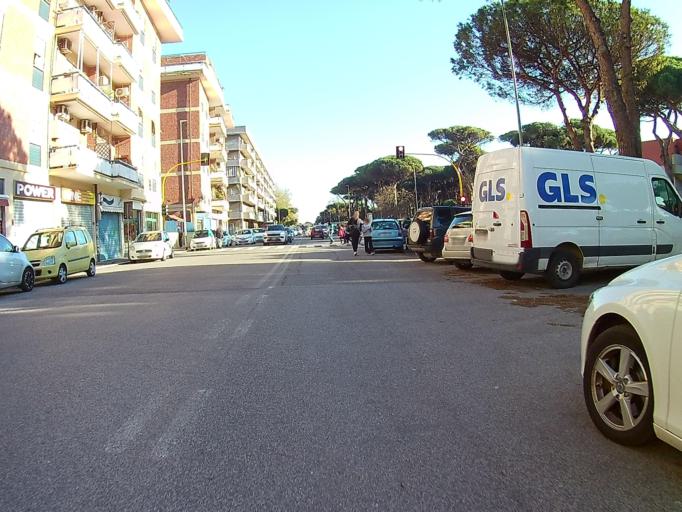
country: IT
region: Latium
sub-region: Citta metropolitana di Roma Capitale
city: Lido di Ostia
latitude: 41.7349
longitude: 12.2954
